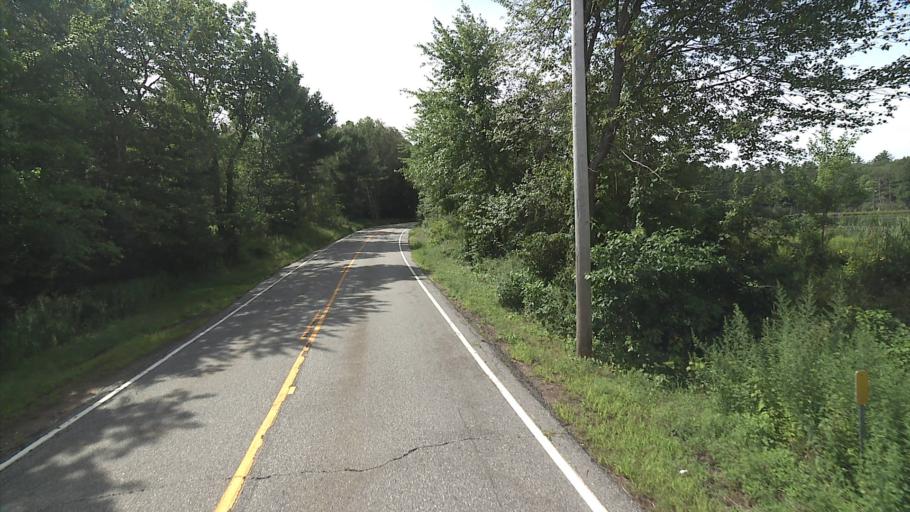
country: US
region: Massachusetts
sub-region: Hampden County
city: Holland
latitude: 41.9717
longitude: -72.1124
